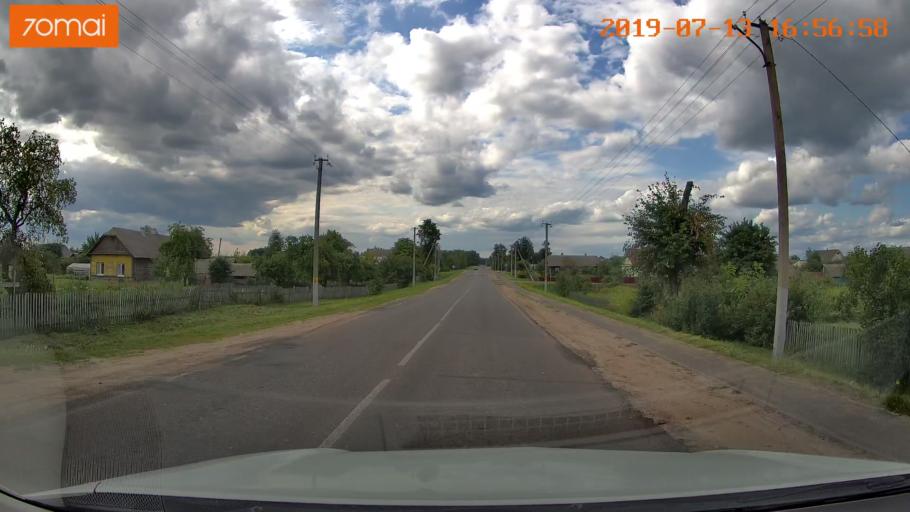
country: BY
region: Mogilev
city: Kirawsk
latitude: 53.2764
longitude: 29.4558
